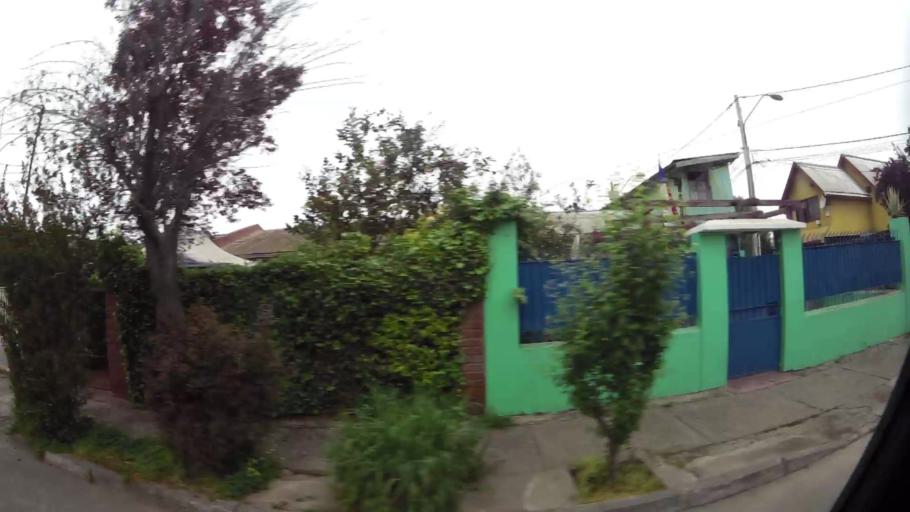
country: CL
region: Santiago Metropolitan
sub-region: Provincia de Santiago
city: Santiago
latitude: -33.4947
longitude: -70.6347
